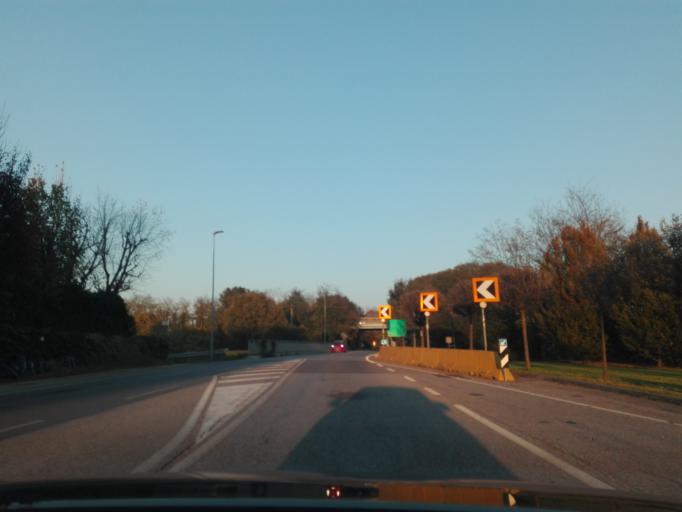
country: IT
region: Lombardy
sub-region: Provincia di Mantova
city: Mottella
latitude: 45.1532
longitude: 10.8368
